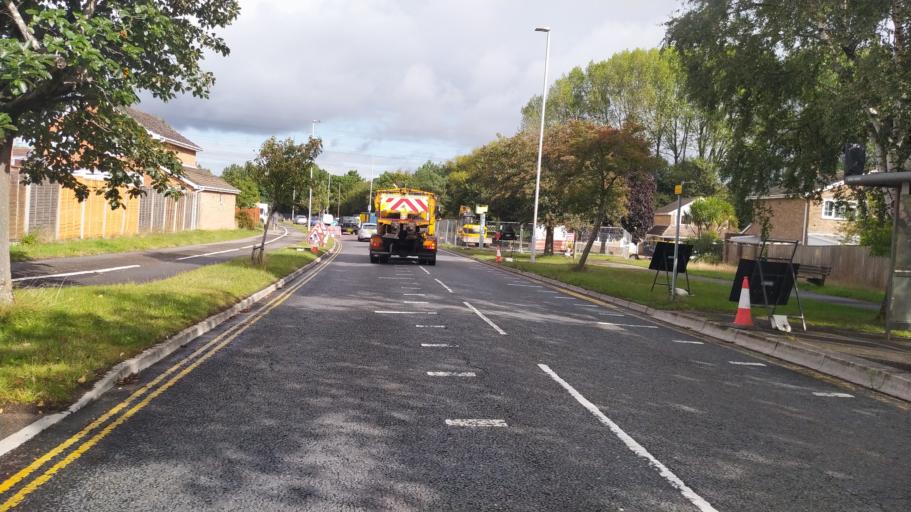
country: GB
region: England
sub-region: Poole
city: Canford Heath
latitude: 50.7468
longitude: -1.9631
